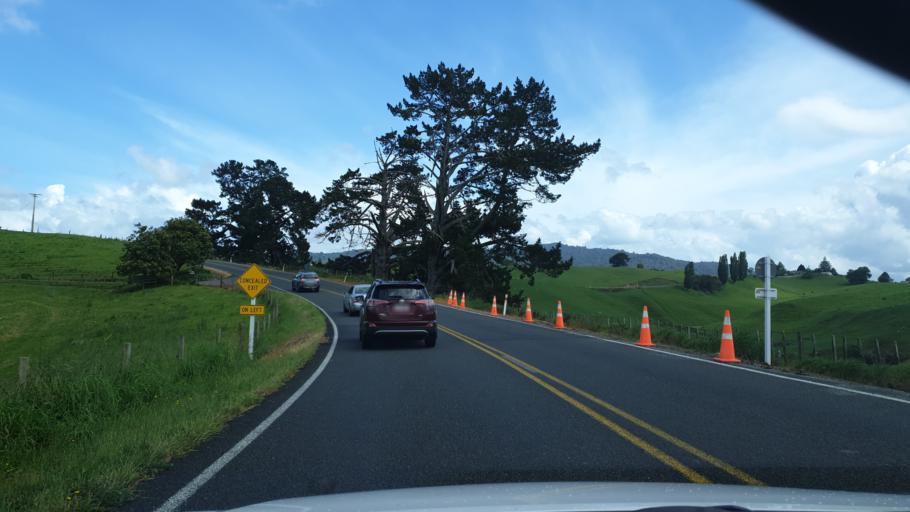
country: NZ
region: Waikato
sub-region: Matamata-Piako District
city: Matamata
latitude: -37.8783
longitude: 175.6887
